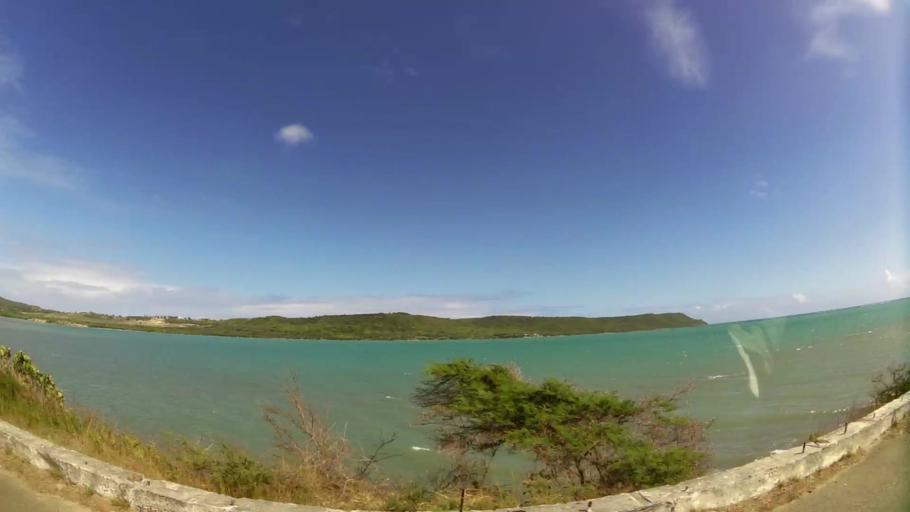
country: AG
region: Saint Paul
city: Falmouth
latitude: 17.0333
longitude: -61.7418
